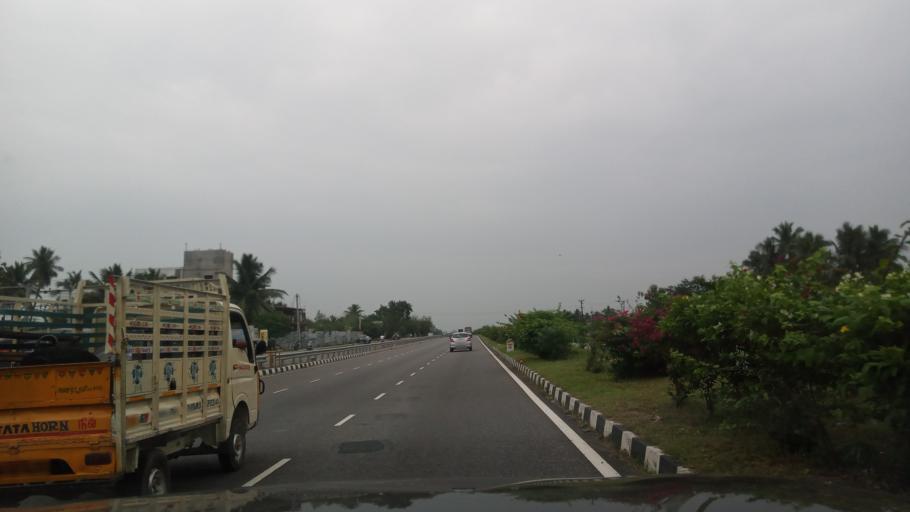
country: IN
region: Tamil Nadu
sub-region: Vellore
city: Pallikondai
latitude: 12.9121
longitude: 79.0028
